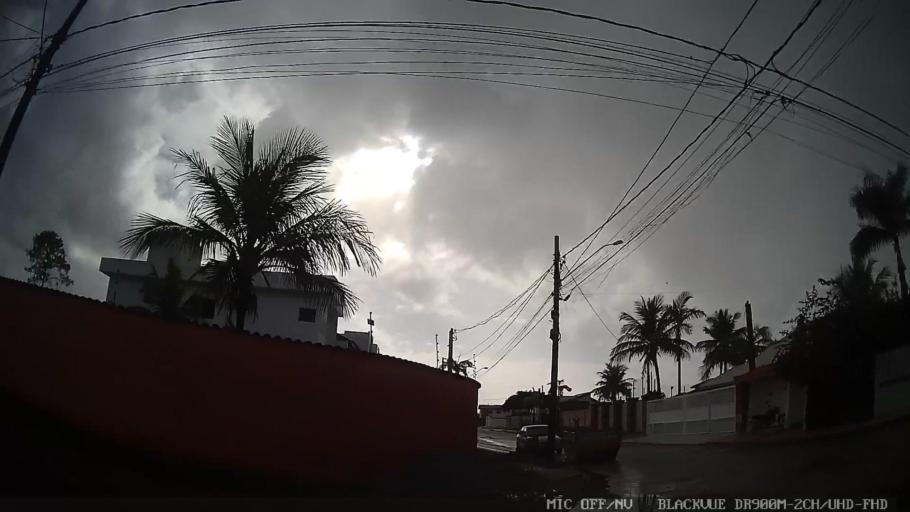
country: BR
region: Sao Paulo
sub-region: Itanhaem
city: Itanhaem
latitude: -24.2022
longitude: -46.8344
